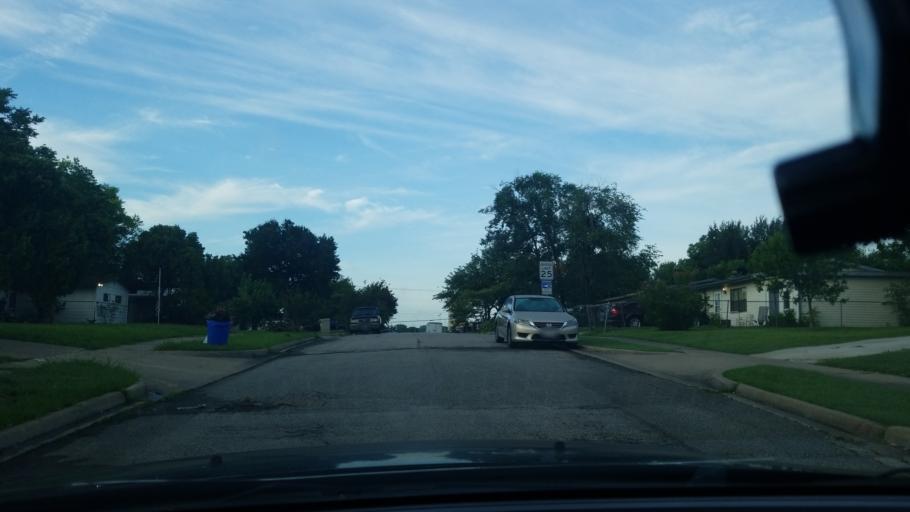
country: US
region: Texas
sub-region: Dallas County
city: Mesquite
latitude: 32.7679
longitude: -96.6306
